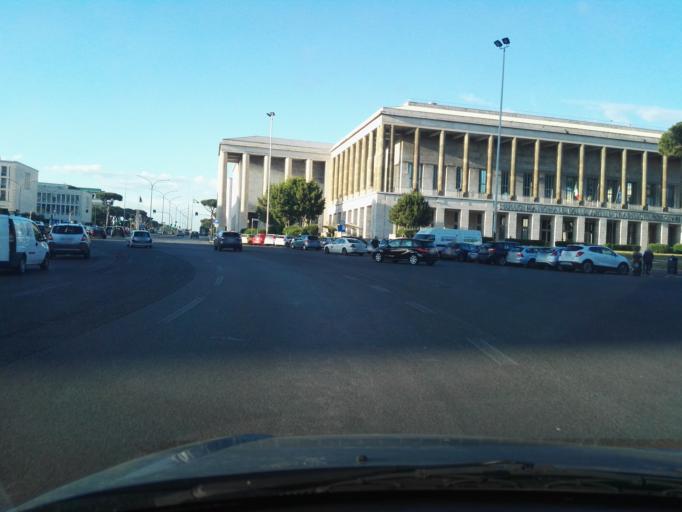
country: IT
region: Latium
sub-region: Citta metropolitana di Roma Capitale
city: Selcetta
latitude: 41.8333
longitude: 12.4710
